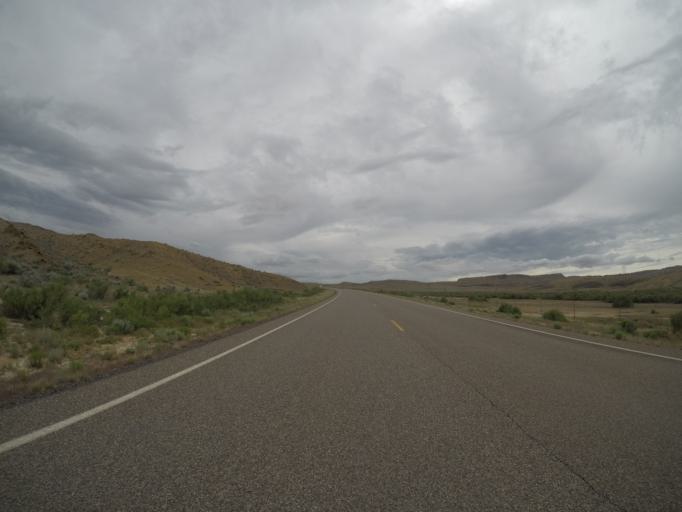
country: US
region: Wyoming
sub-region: Big Horn County
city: Lovell
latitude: 44.9546
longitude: -108.2936
